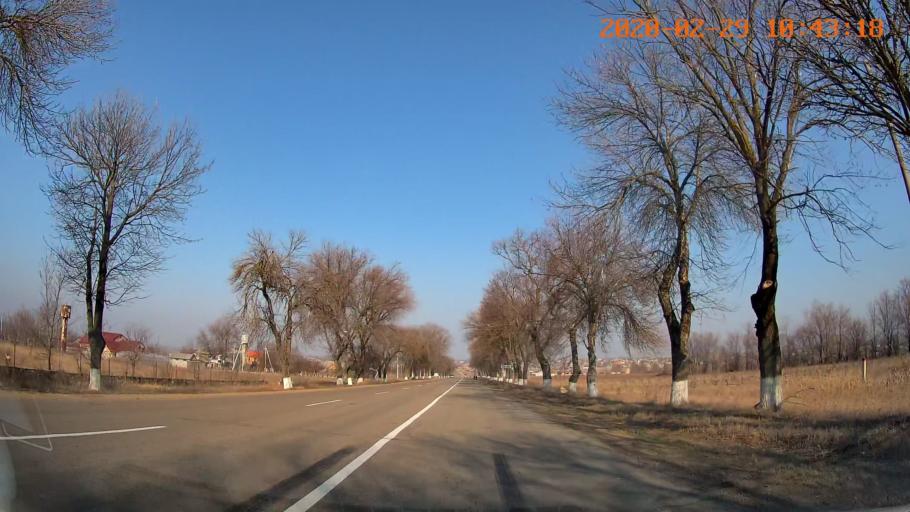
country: MD
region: Telenesti
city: Grigoriopol
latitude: 47.0597
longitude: 29.4041
